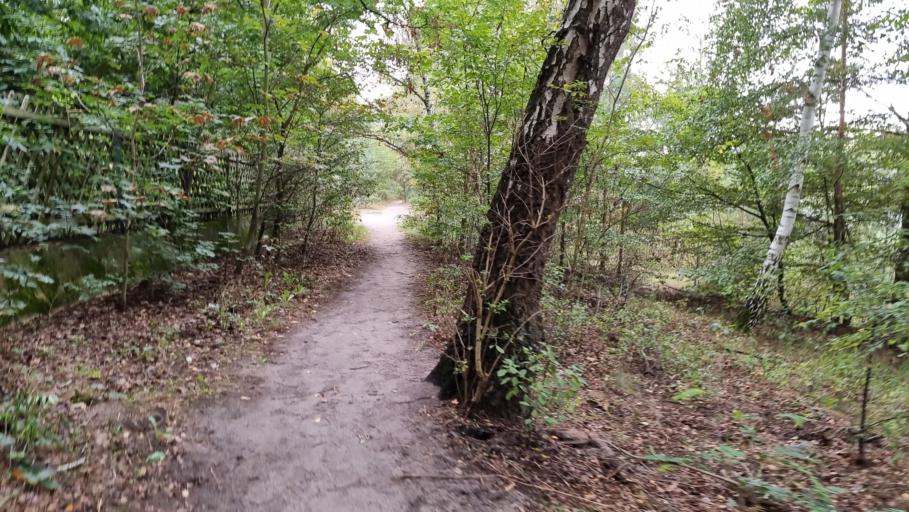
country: DE
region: Lower Saxony
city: Garbsen
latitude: 52.4188
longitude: 9.5527
